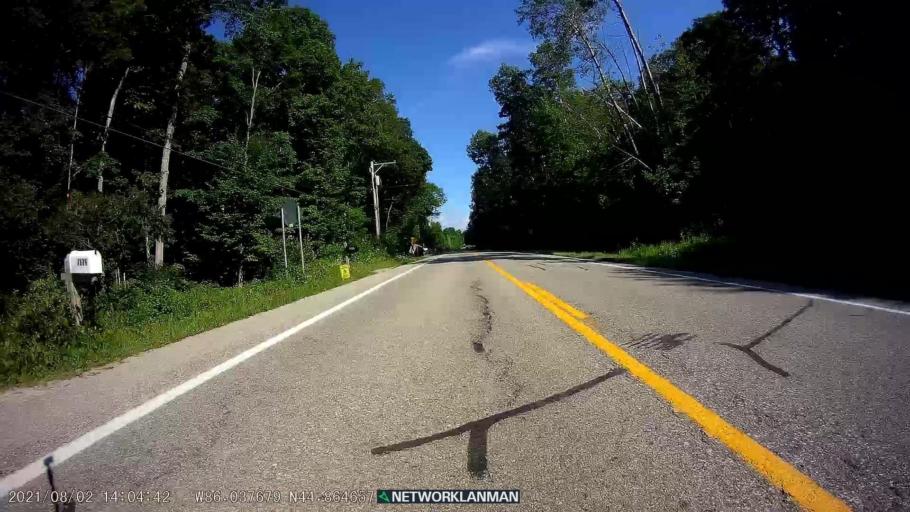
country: US
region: Michigan
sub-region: Benzie County
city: Beulah
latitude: 44.8647
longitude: -86.0378
